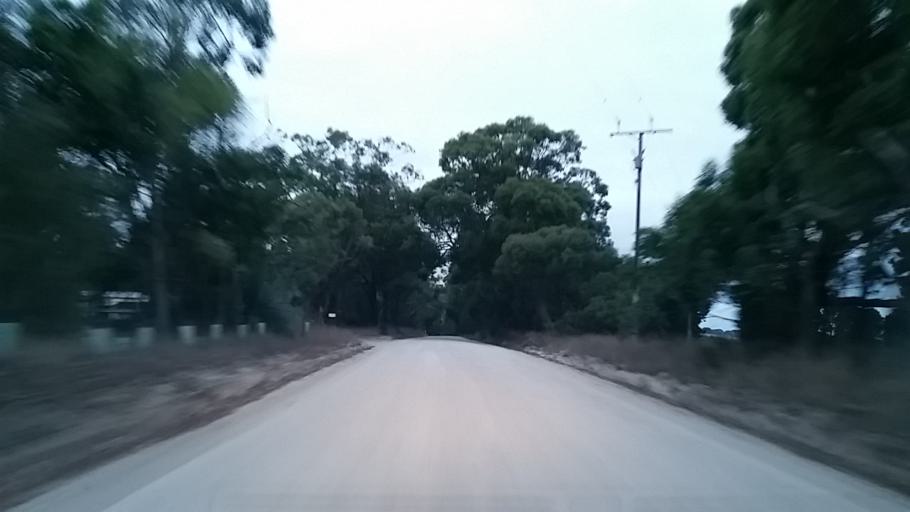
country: AU
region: South Australia
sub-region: Yankalilla
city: Normanville
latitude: -35.6107
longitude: 138.1691
